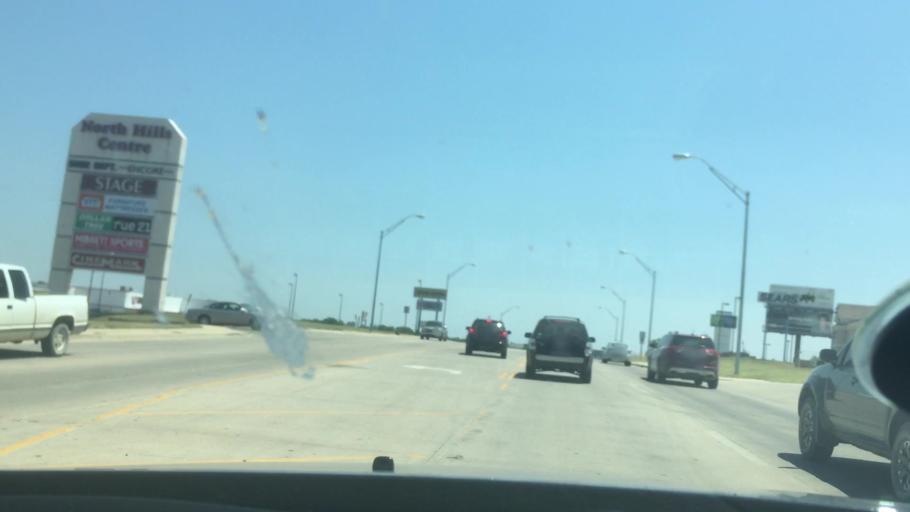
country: US
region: Oklahoma
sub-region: Pontotoc County
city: Ada
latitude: 34.7902
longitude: -96.6649
